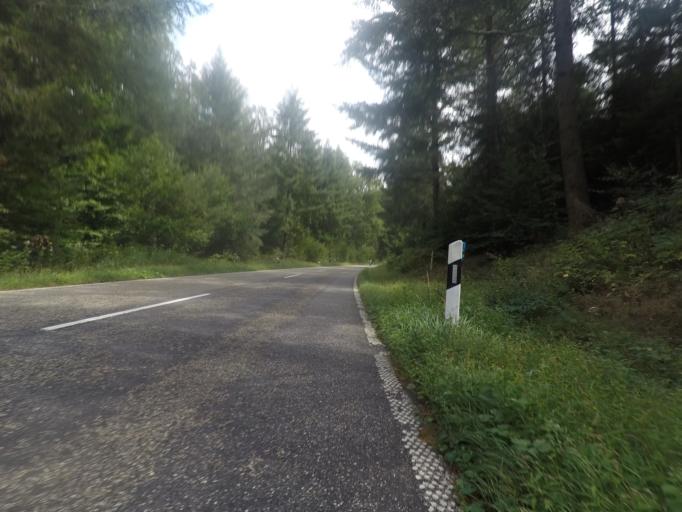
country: DE
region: Baden-Wuerttemberg
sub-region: Karlsruhe Region
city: Ettlingen
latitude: 48.8685
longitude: 8.4167
